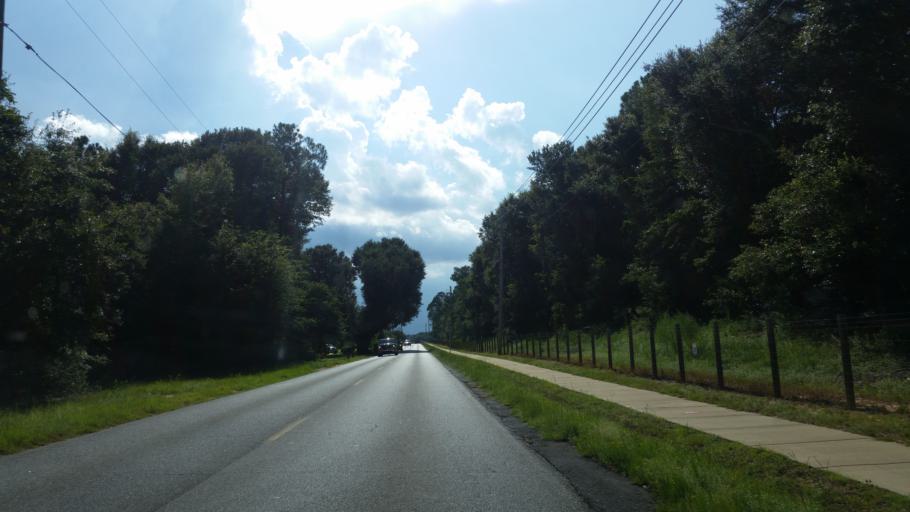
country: US
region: Florida
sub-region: Santa Rosa County
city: Pace
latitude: 30.6184
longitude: -87.1435
